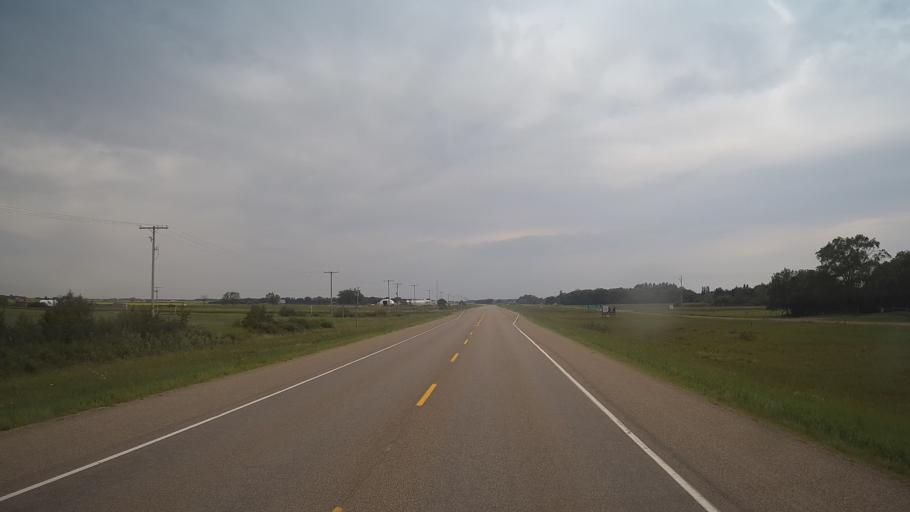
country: CA
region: Saskatchewan
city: Langham
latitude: 52.1289
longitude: -107.2134
